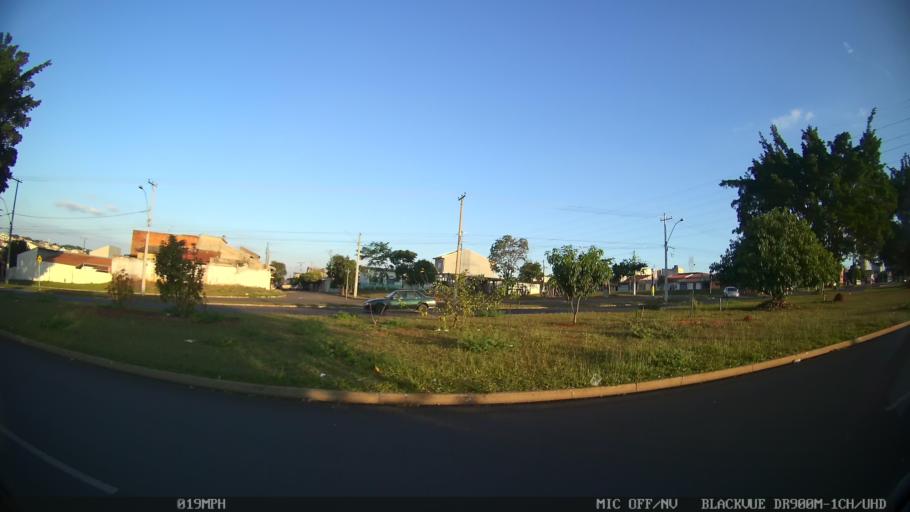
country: BR
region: Sao Paulo
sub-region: Santa Barbara D'Oeste
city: Santa Barbara d'Oeste
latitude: -22.7368
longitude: -47.3956
